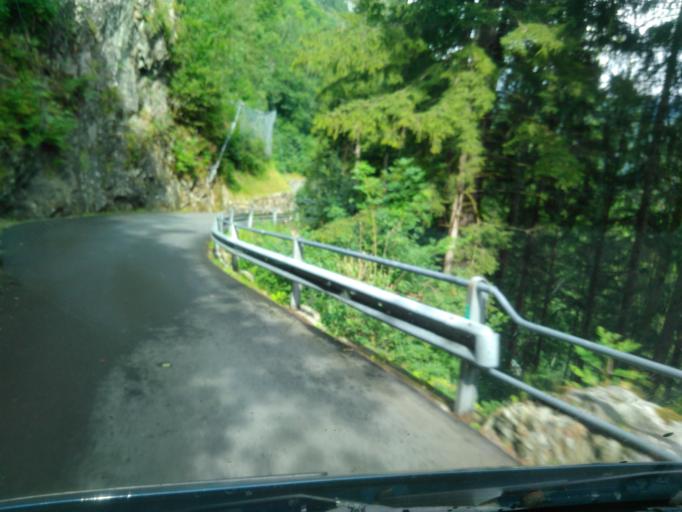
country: CH
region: Bern
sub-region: Interlaken-Oberhasli District
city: Meiringen
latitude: 46.6990
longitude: 8.2252
